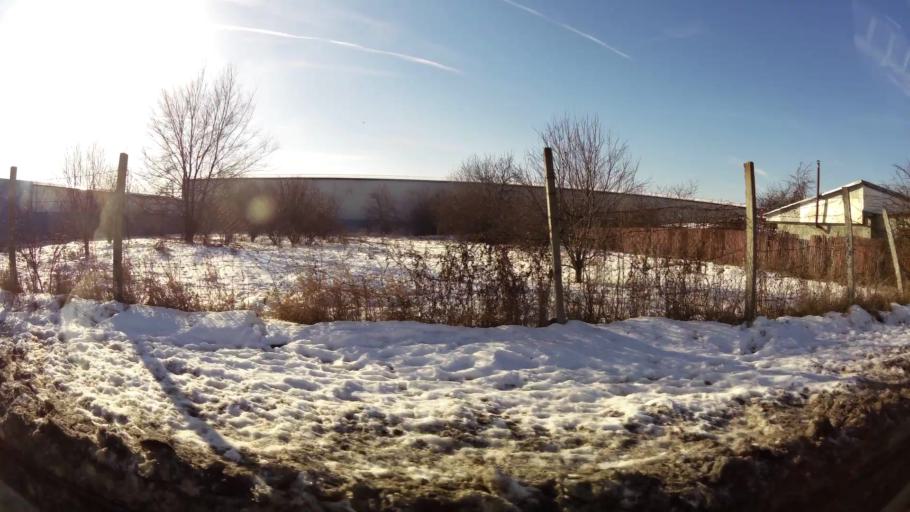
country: RO
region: Ilfov
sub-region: Comuna Fundeni-Dobroesti
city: Fundeni
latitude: 44.4776
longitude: 26.1388
